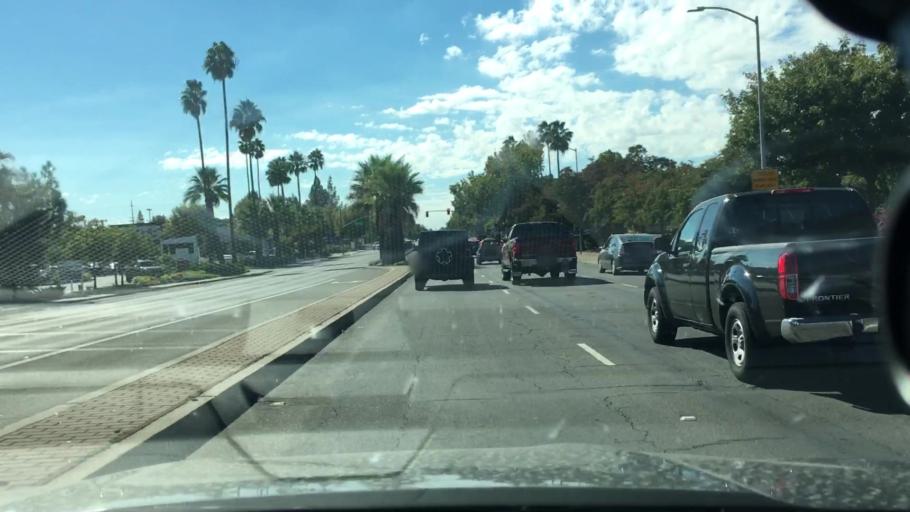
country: US
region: California
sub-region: Sacramento County
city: Arden-Arcade
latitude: 38.6083
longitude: -121.3831
